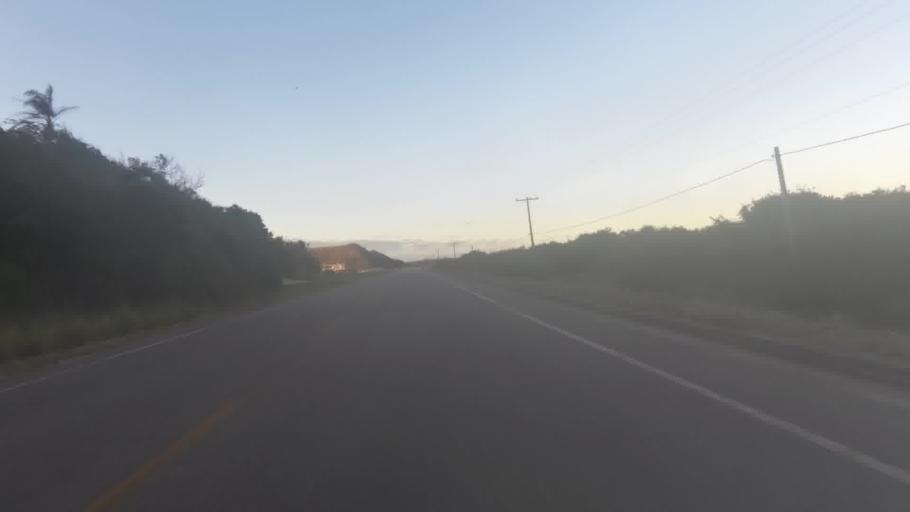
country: BR
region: Espirito Santo
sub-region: Marataizes
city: Marataizes
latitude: -21.1777
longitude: -40.9209
